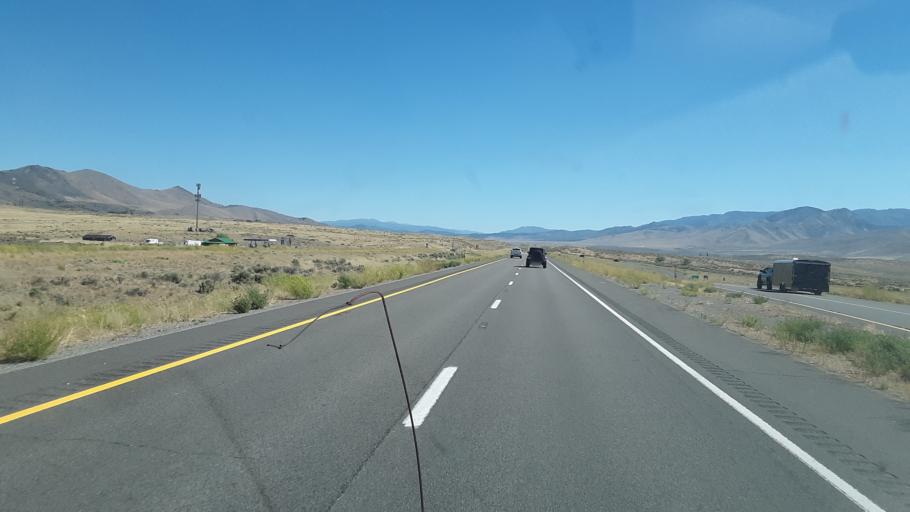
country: US
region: Nevada
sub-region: Washoe County
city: Cold Springs
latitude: 39.7789
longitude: -120.0388
